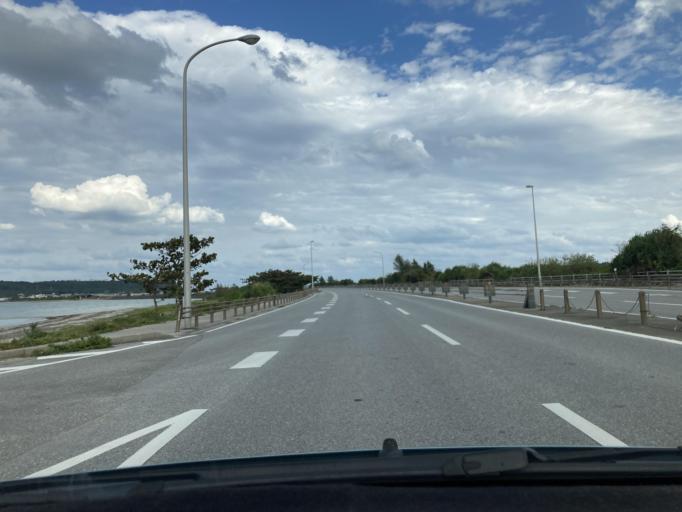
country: JP
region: Okinawa
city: Katsuren-haebaru
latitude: 26.3317
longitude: 127.9300
